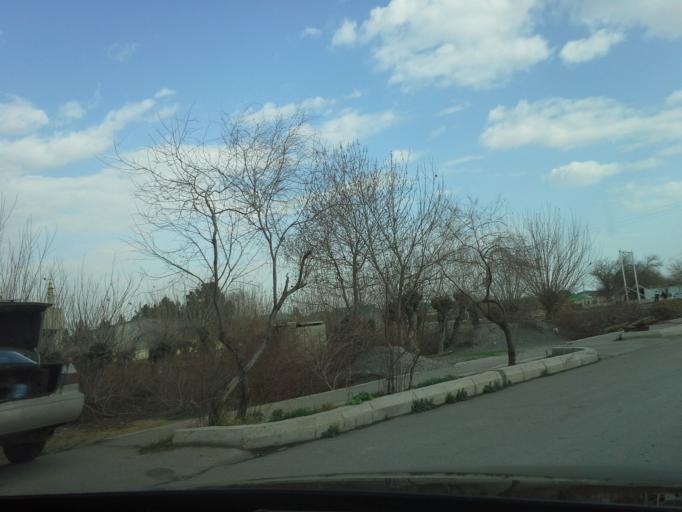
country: TM
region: Ahal
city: Ashgabat
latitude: 37.9899
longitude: 58.2869
